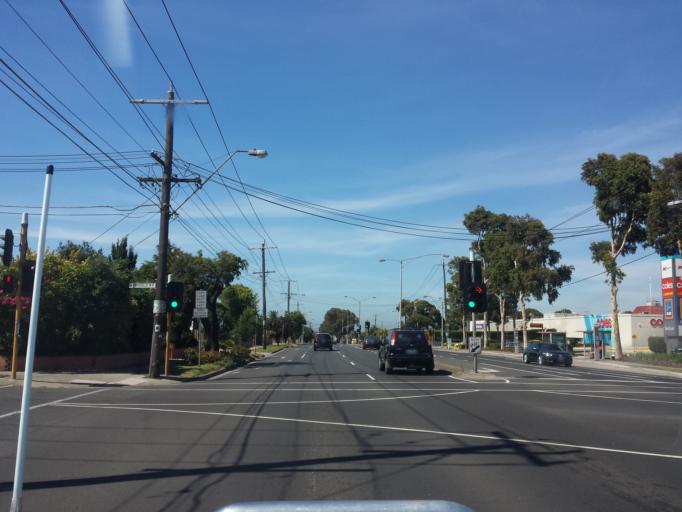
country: AU
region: Victoria
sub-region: Hobsons Bay
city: Altona North
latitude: -37.8270
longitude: 144.8490
